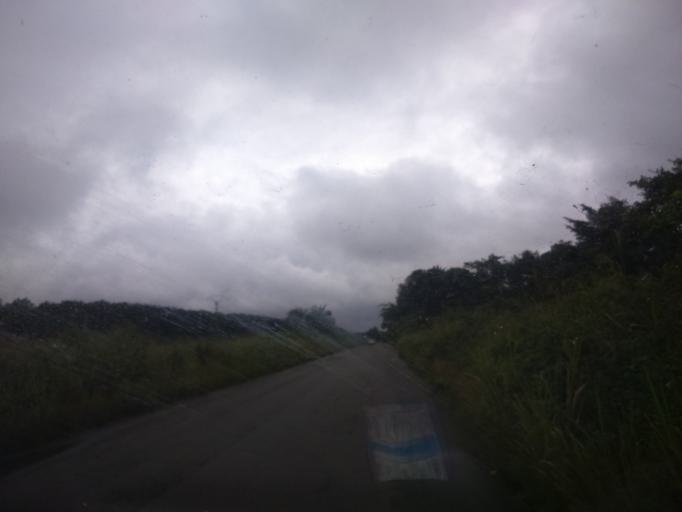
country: CI
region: Sud-Comoe
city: Bonoua
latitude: 5.2814
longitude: -3.4813
